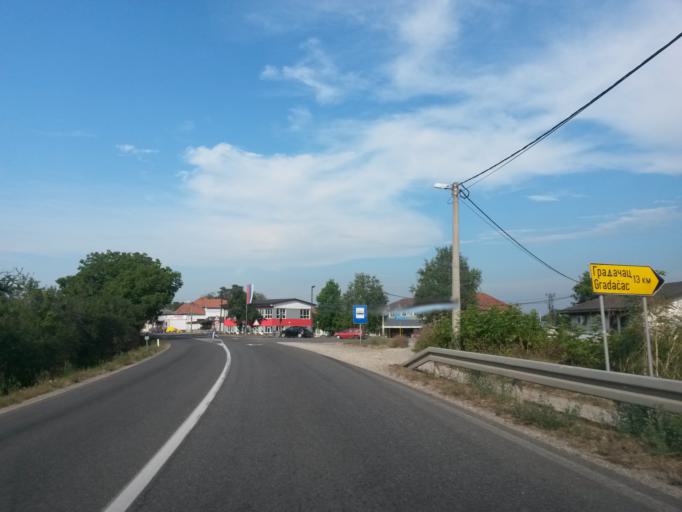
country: BA
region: Republika Srpska
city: Bosanski Samac
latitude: 45.0307
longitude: 18.4343
